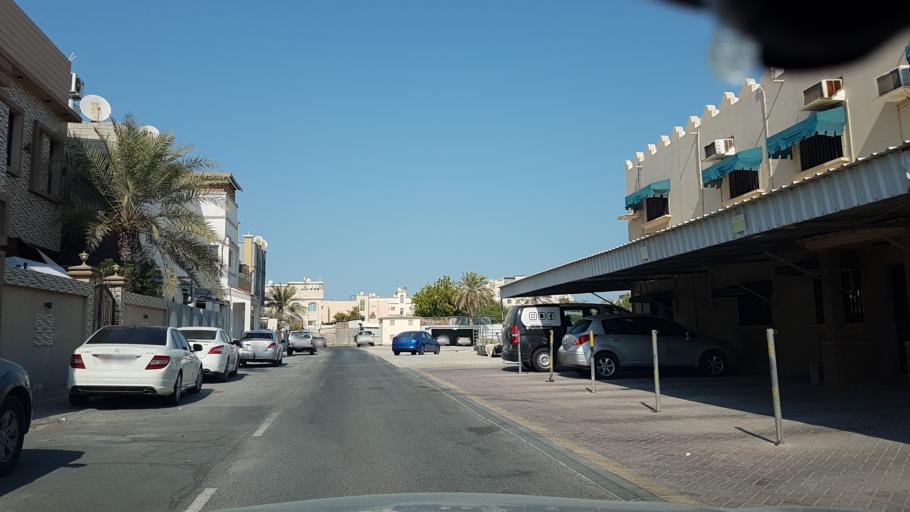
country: BH
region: Muharraq
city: Al Muharraq
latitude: 26.2536
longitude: 50.6278
